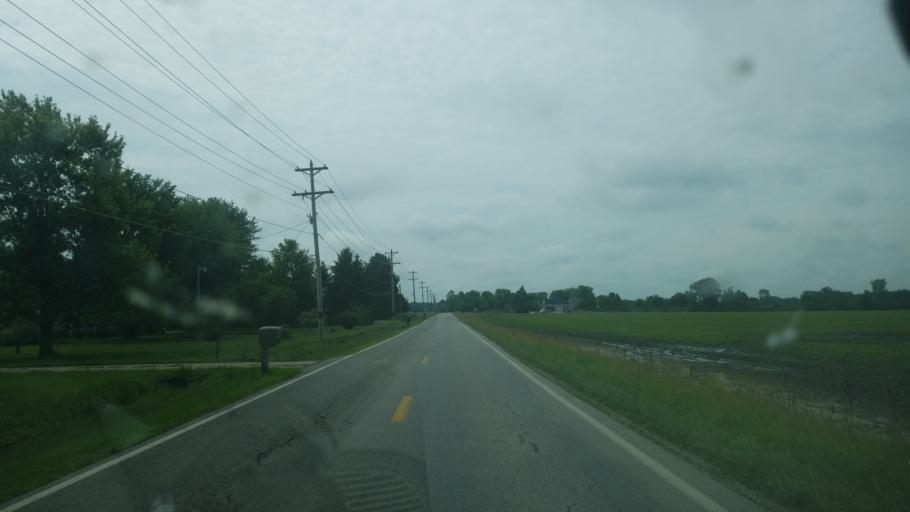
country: US
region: Ohio
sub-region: Franklin County
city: New Albany
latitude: 40.1297
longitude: -82.7615
